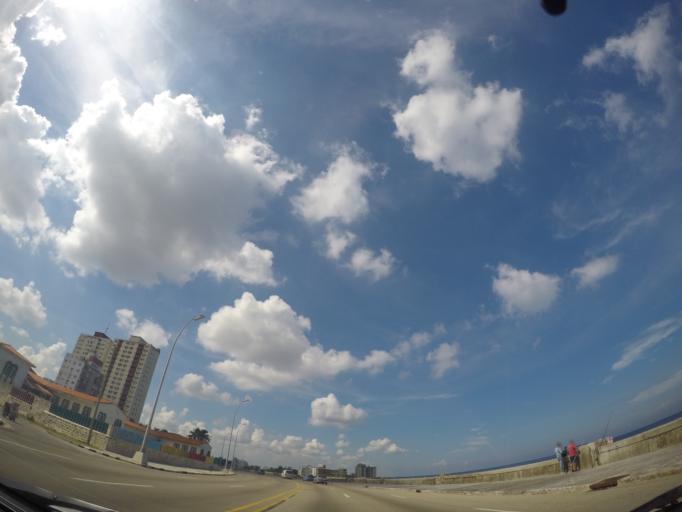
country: CU
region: La Habana
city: Havana
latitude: 23.1378
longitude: -82.4074
